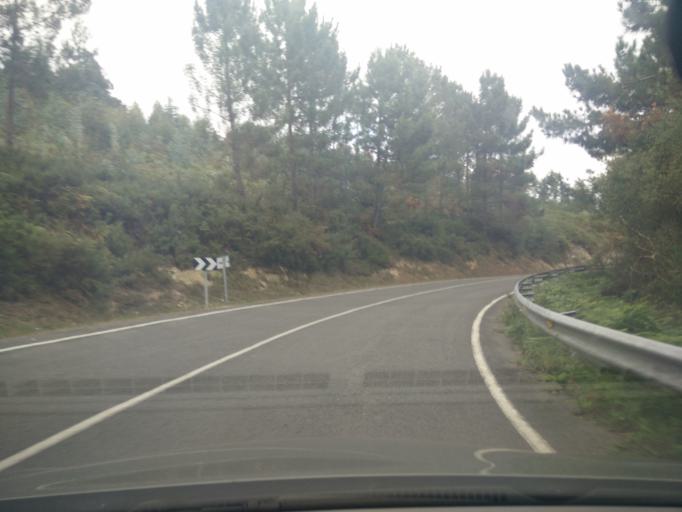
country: ES
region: Galicia
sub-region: Provincia da Coruna
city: Laxe
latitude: 43.2473
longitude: -8.9349
